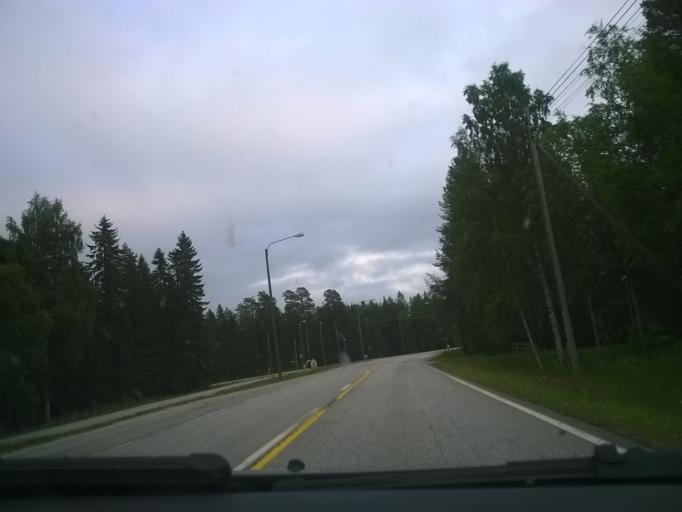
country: FI
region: Kainuu
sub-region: Kehys-Kainuu
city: Kuhmo
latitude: 64.1375
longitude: 29.4530
